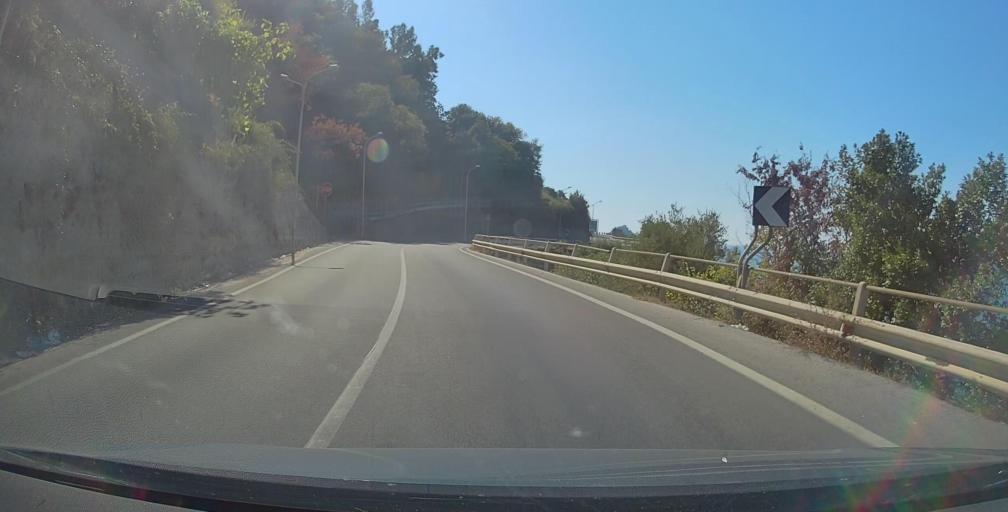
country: IT
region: Sicily
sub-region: Messina
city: Naso
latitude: 38.1533
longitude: 14.7808
